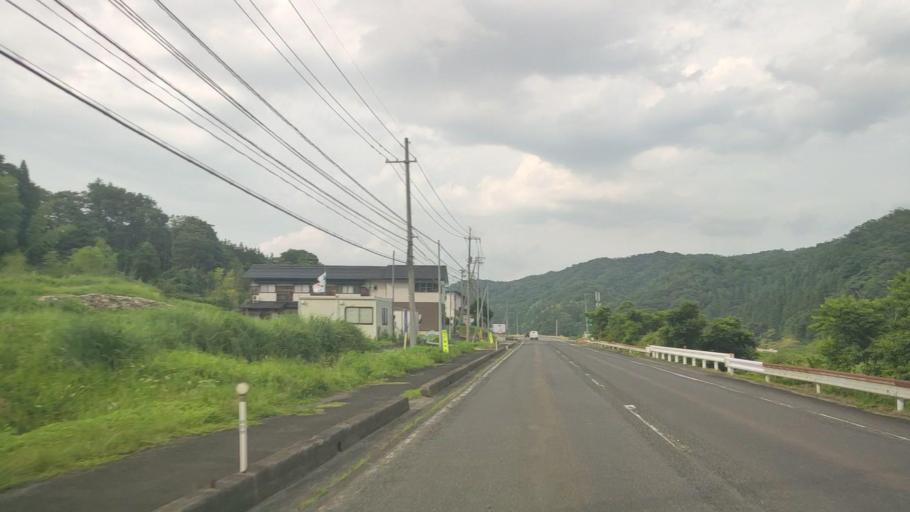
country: JP
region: Tottori
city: Kurayoshi
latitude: 35.3812
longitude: 133.8533
